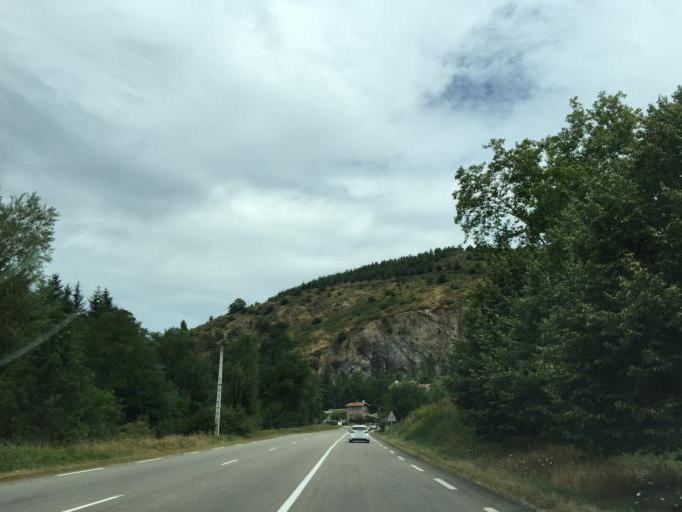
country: FR
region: Rhone-Alpes
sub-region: Departement de la Loire
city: Fraisses
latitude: 45.4059
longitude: 4.2544
